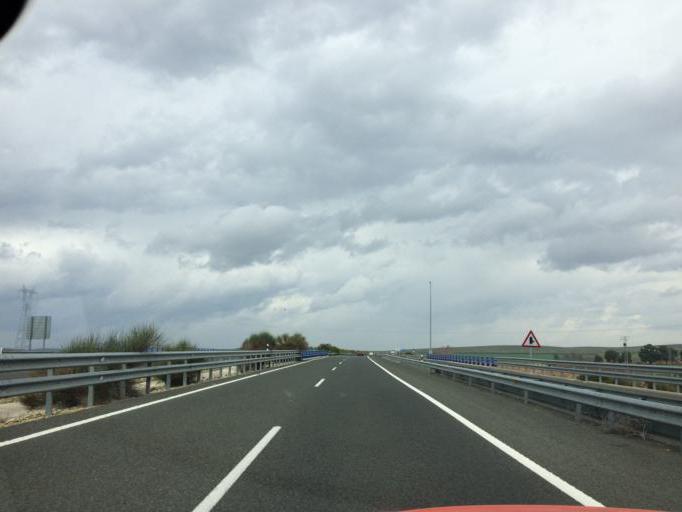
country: ES
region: Andalusia
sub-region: Provincia de Malaga
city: Antequera
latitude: 37.0695
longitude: -4.5292
